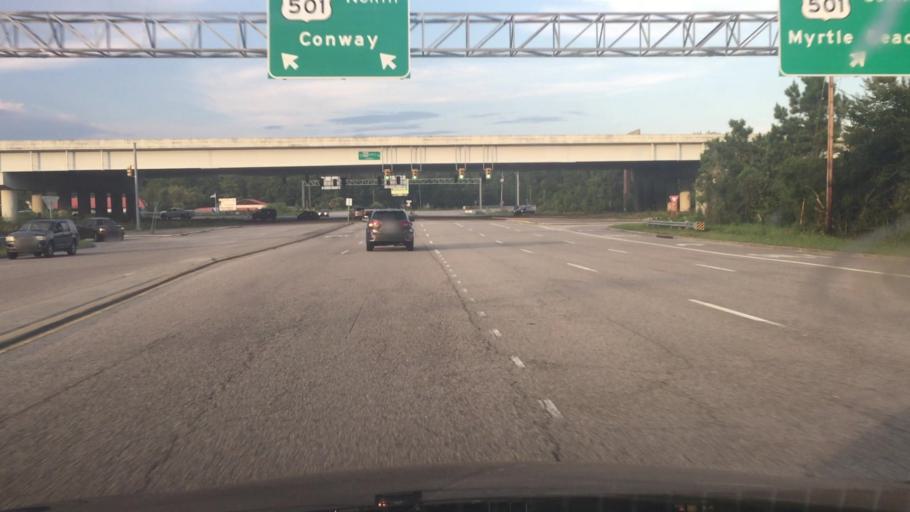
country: US
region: South Carolina
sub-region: Horry County
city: Forestbrook
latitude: 33.7323
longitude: -78.9461
